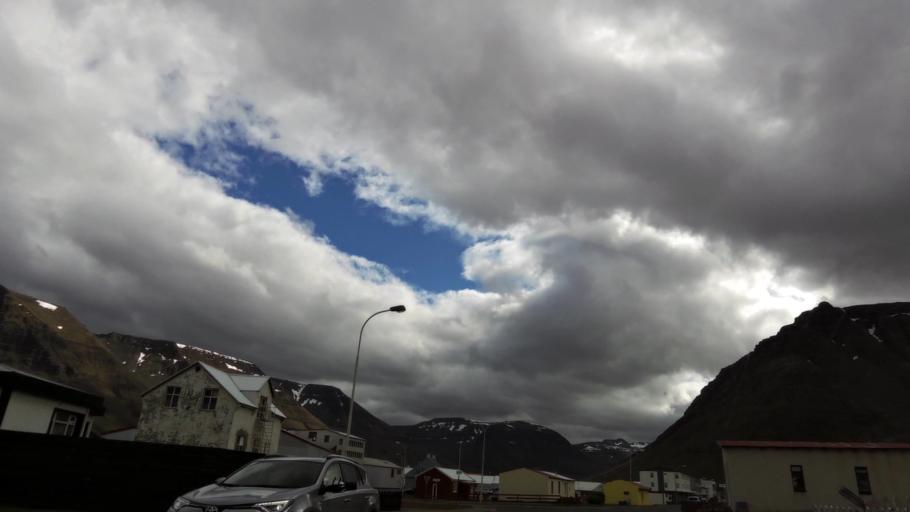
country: IS
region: Westfjords
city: Isafjoerdur
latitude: 66.1606
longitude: -23.2475
